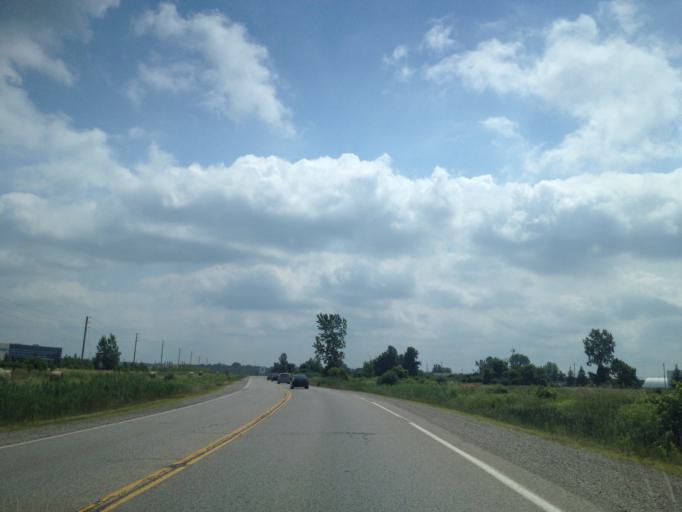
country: CA
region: Ontario
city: London
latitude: 43.0274
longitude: -81.1730
